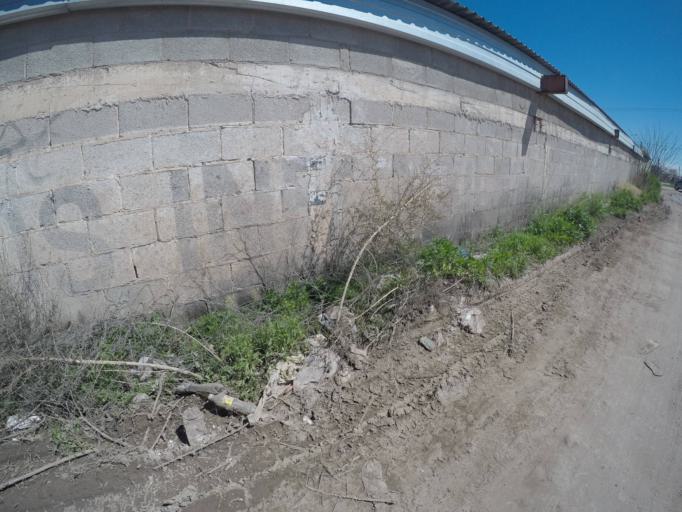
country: US
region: Texas
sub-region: El Paso County
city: Socorro Mission Number 1 Colonia
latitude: 31.6063
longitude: -106.3108
